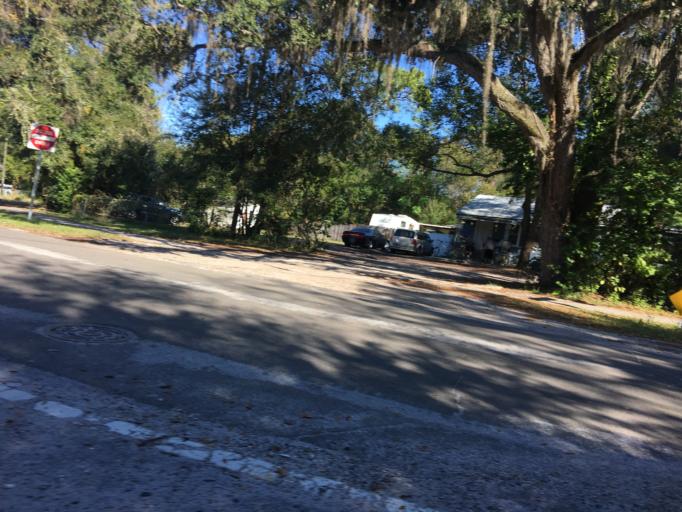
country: US
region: Florida
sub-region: Hillsborough County
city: University
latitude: 28.0398
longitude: -82.4398
